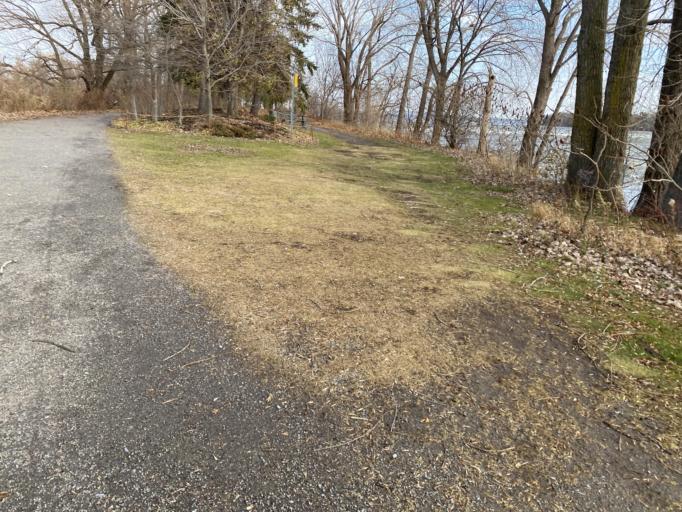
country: CA
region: Quebec
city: Saint-Raymond
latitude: 45.4253
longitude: -73.5927
